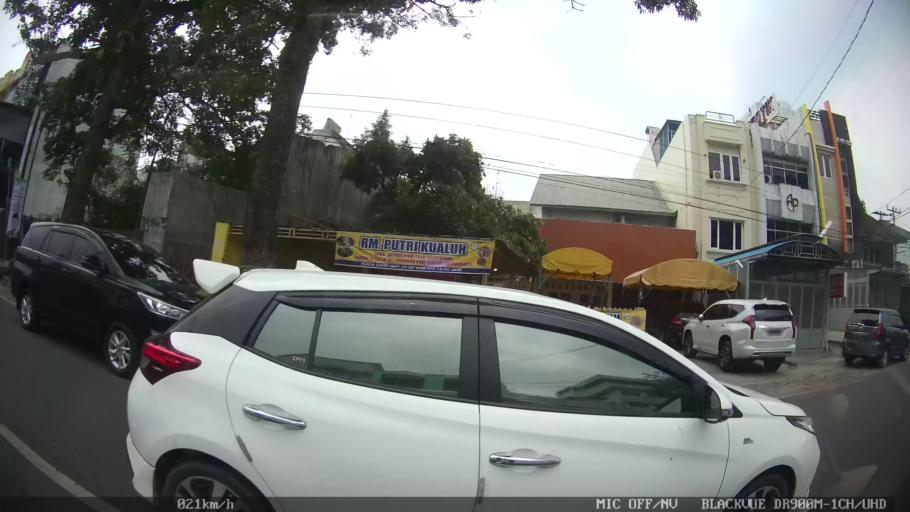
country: ID
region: North Sumatra
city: Medan
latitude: 3.5795
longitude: 98.6860
